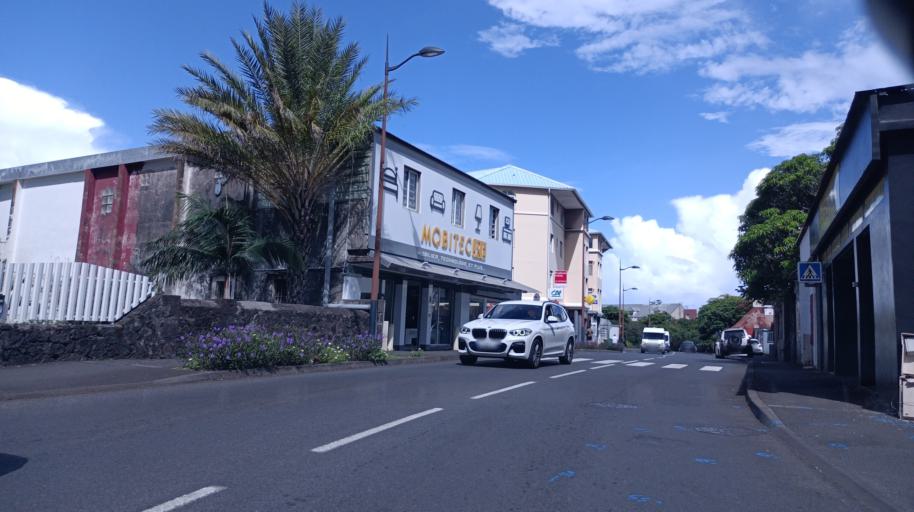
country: RE
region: Reunion
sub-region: Reunion
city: Saint-Joseph
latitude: -21.3803
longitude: 55.6155
